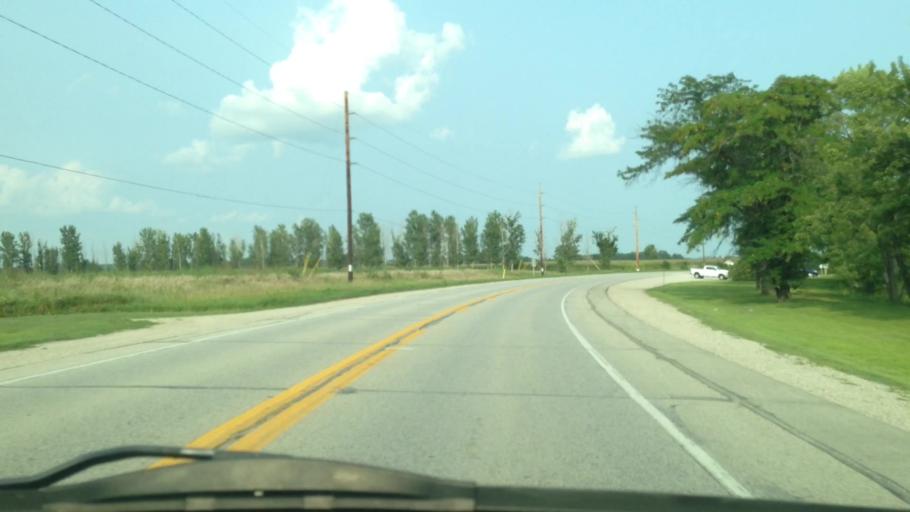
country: US
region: Iowa
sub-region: Benton County
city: Walford
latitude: 41.8033
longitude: -91.8895
